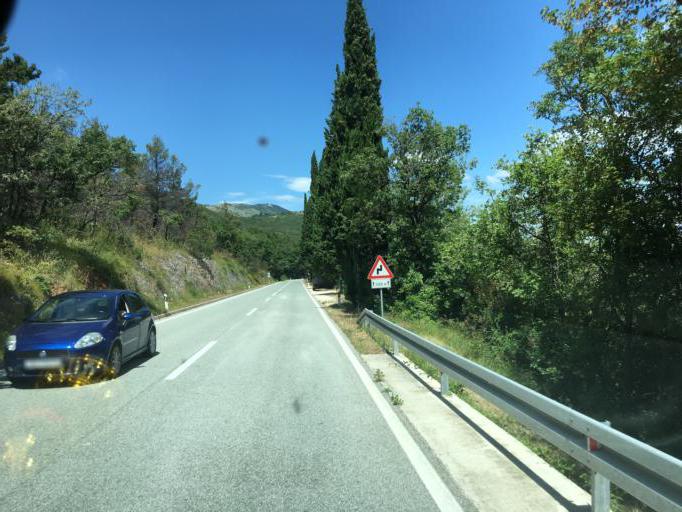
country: HR
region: Istarska
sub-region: Grad Labin
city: Rabac
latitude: 45.1293
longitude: 14.2045
